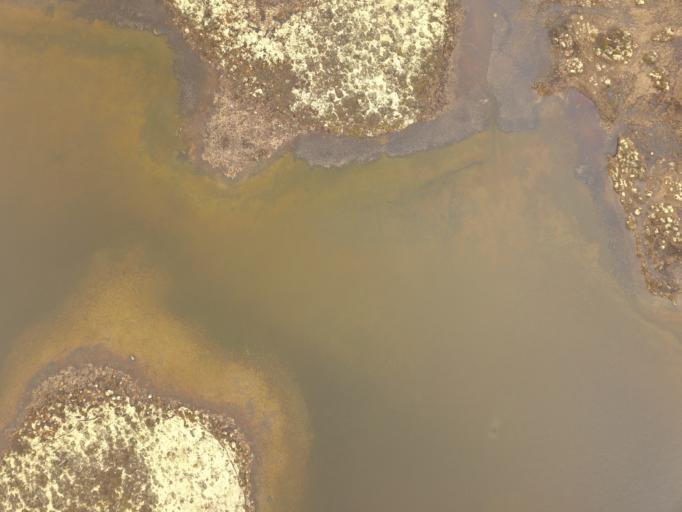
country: NO
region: Hedmark
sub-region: Folldal
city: Folldal
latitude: 62.2278
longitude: 9.6455
